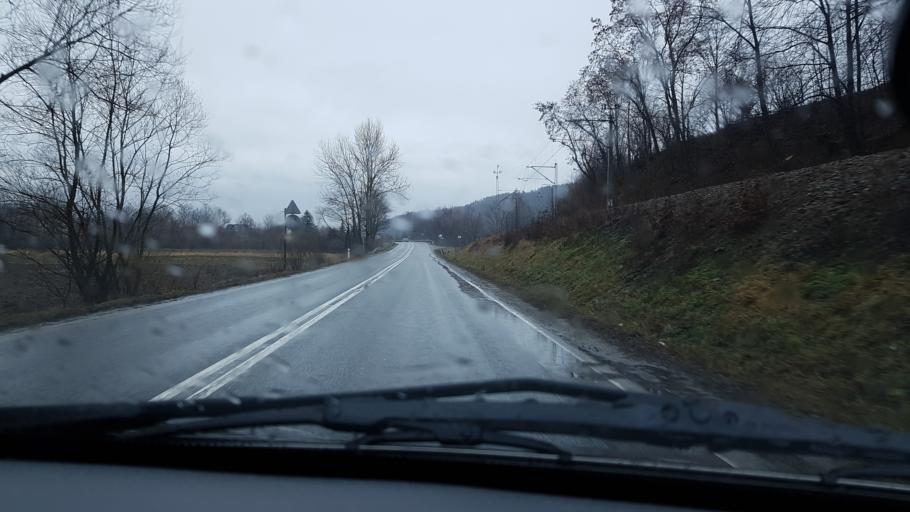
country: PL
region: Lesser Poland Voivodeship
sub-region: Powiat suski
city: Juszczyn
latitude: 49.6921
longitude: 19.7210
